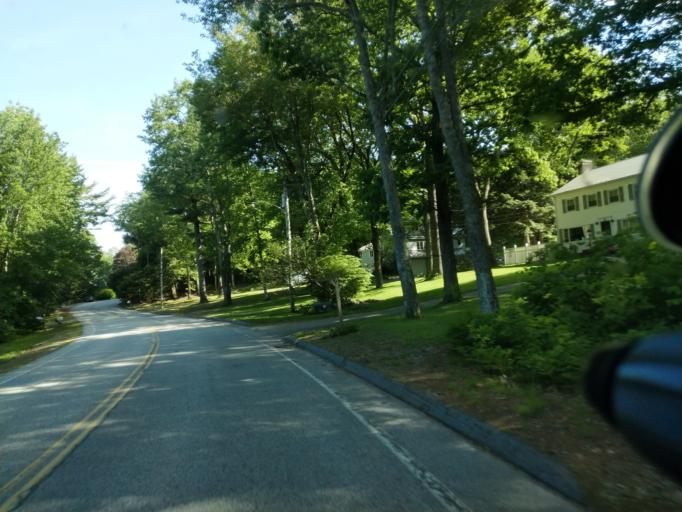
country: US
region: Maine
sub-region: Cumberland County
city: Falmouth
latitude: 43.7413
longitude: -70.3052
